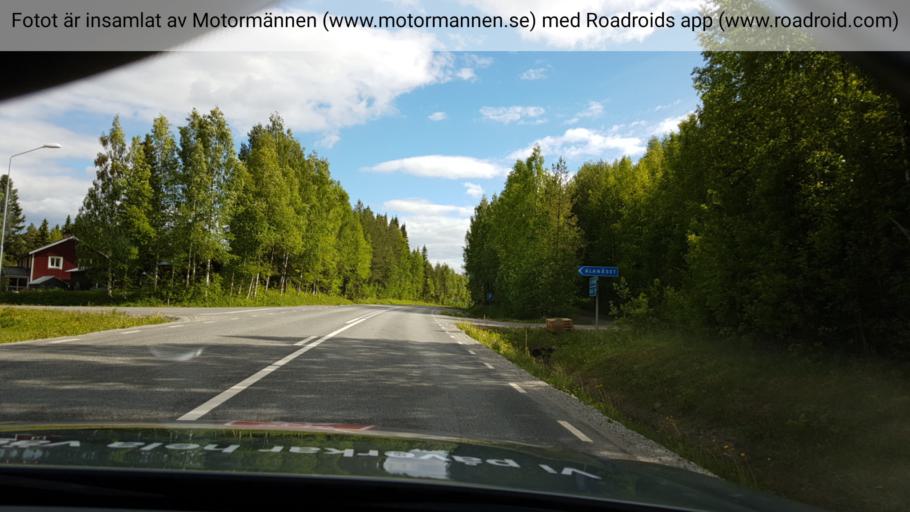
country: SE
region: Jaemtland
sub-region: Stroemsunds Kommun
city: Stroemsund
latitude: 64.1651
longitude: 15.6750
